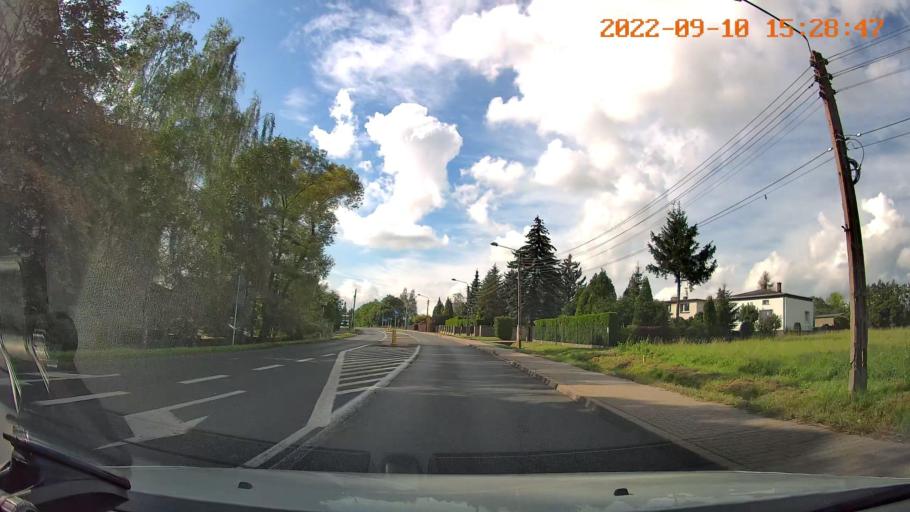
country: PL
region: Lesser Poland Voivodeship
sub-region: Powiat oswiecimski
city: Babice
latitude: 50.0778
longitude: 19.1752
